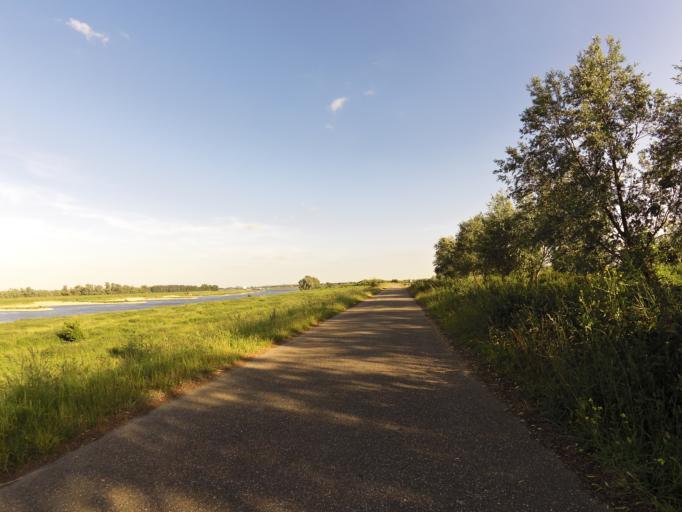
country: NL
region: Gelderland
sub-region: Gemeente Duiven
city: Duiven
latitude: 51.8878
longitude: 6.0236
